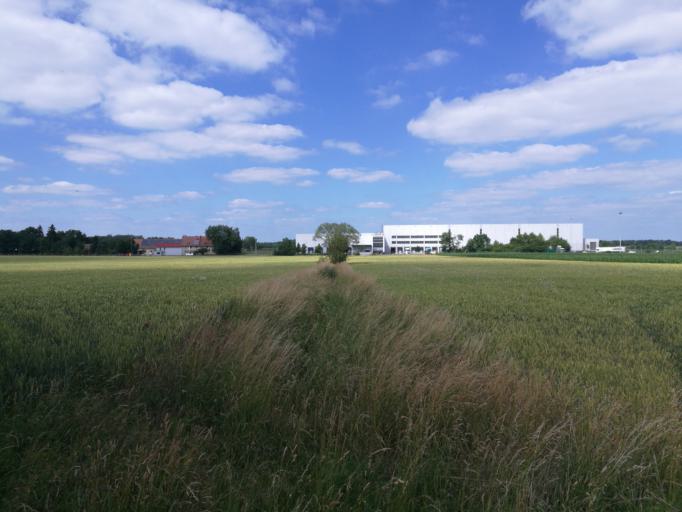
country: DE
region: Bavaria
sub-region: Regierungsbezirk Mittelfranken
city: Seukendorf
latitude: 49.4937
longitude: 10.9047
